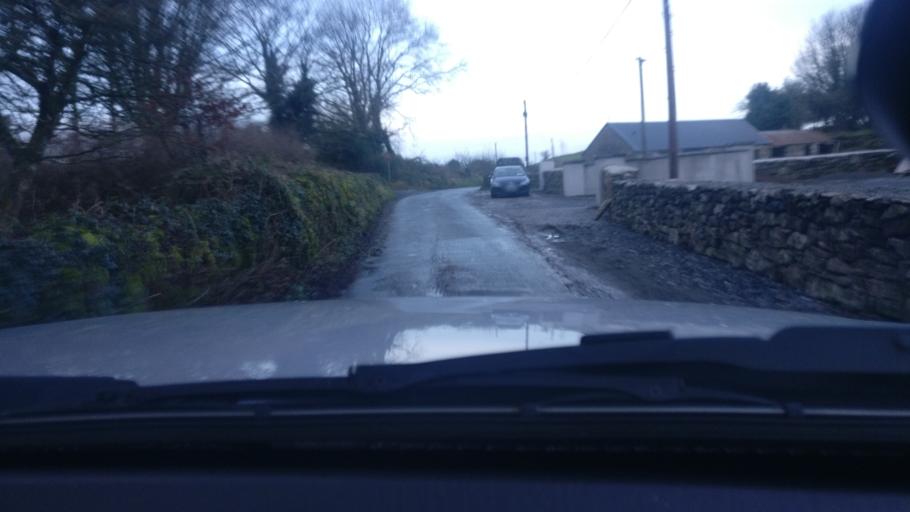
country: IE
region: Connaught
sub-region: County Galway
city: Loughrea
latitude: 53.1654
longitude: -8.5797
